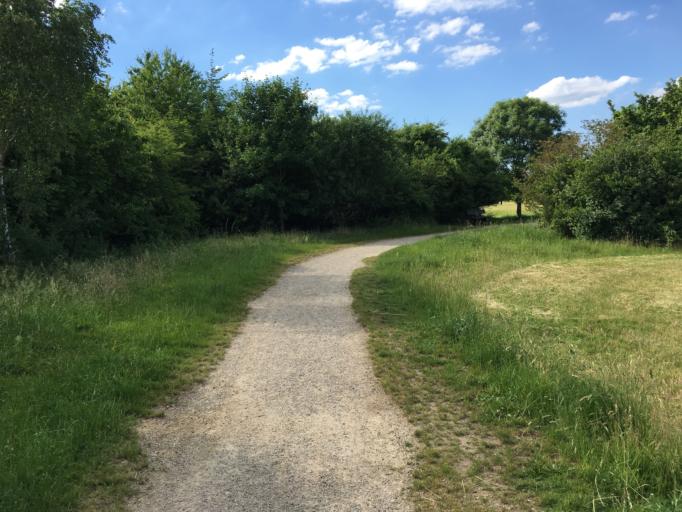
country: DE
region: North Rhine-Westphalia
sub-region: Regierungsbezirk Koln
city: Dueren
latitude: 50.7829
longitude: 6.4743
